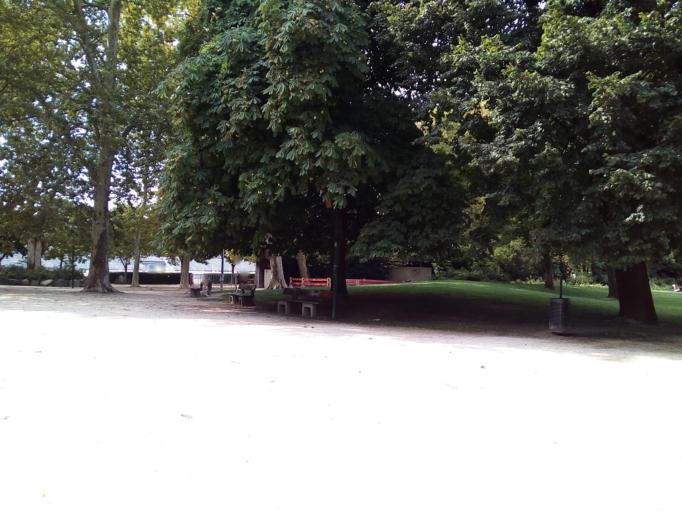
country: FR
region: Rhone-Alpes
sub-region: Departement de l'Isere
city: La Tronche
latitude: 45.1857
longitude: 5.7380
